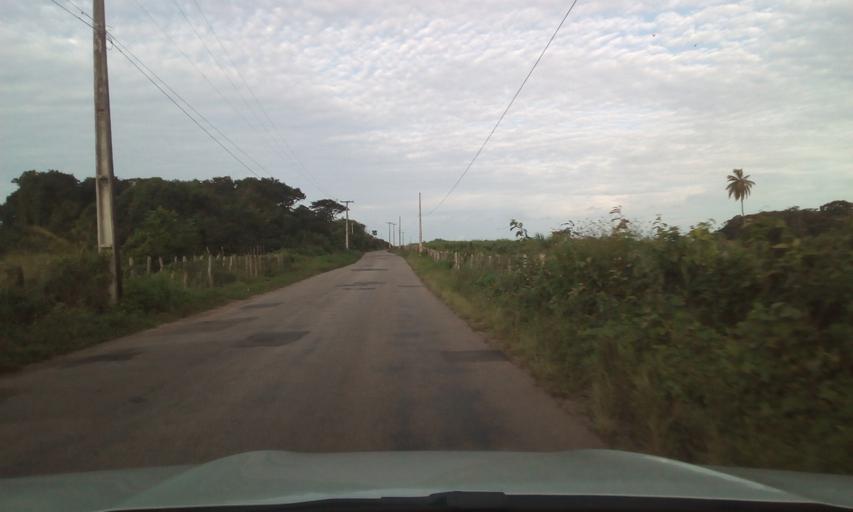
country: BR
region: Paraiba
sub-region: Conde
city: Conde
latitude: -7.2211
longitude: -34.8308
